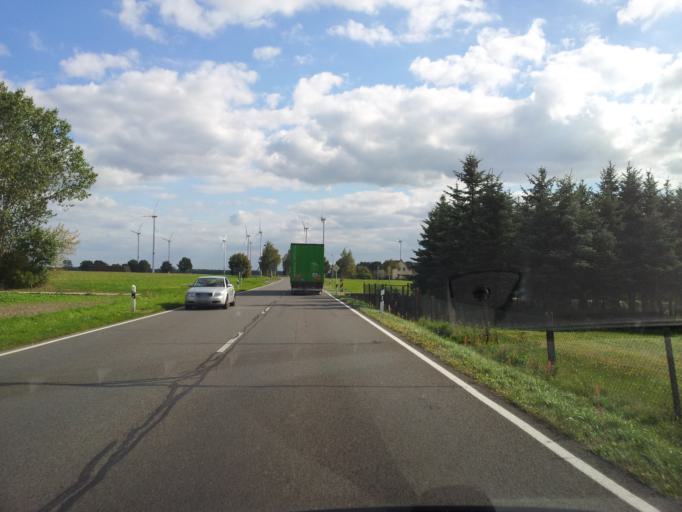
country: DE
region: Brandenburg
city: Sallgast
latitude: 51.6081
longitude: 13.8643
